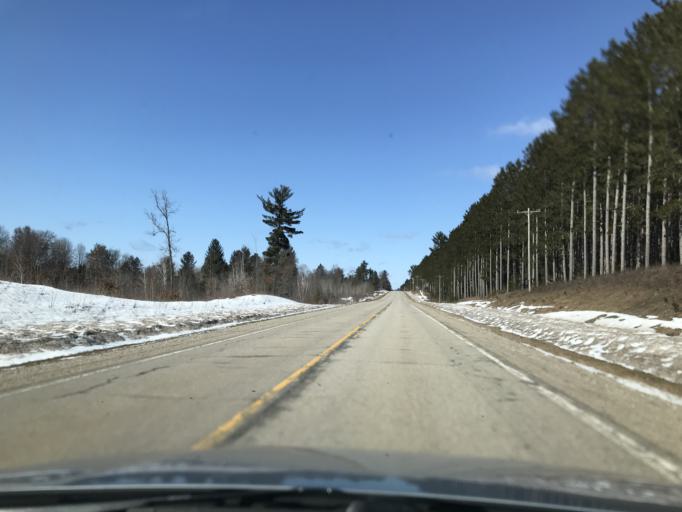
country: US
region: Wisconsin
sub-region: Marinette County
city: Niagara
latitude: 45.3792
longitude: -88.0999
